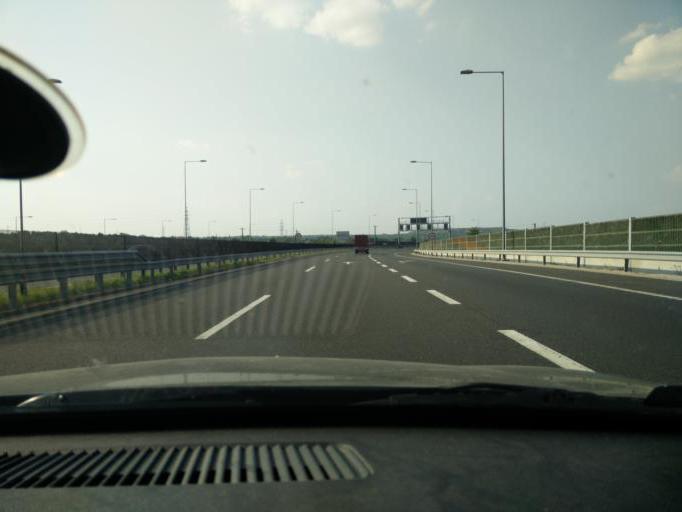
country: HU
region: Pest
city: Diosd
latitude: 47.3956
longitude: 18.9692
